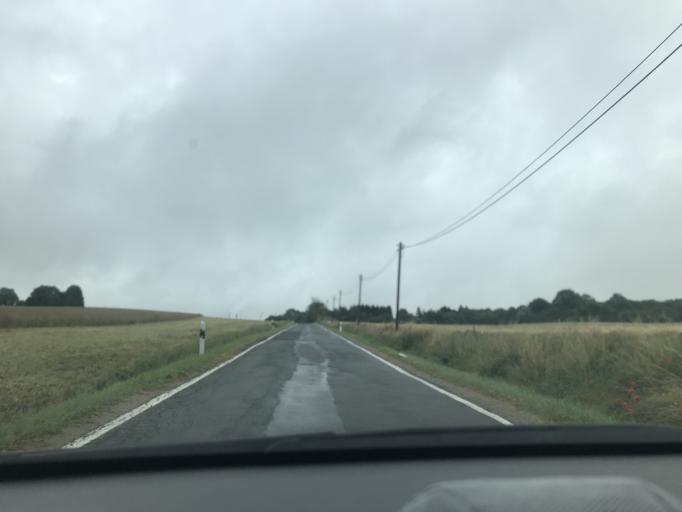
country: DE
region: Thuringia
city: Geisleden
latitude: 51.3182
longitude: 10.1917
